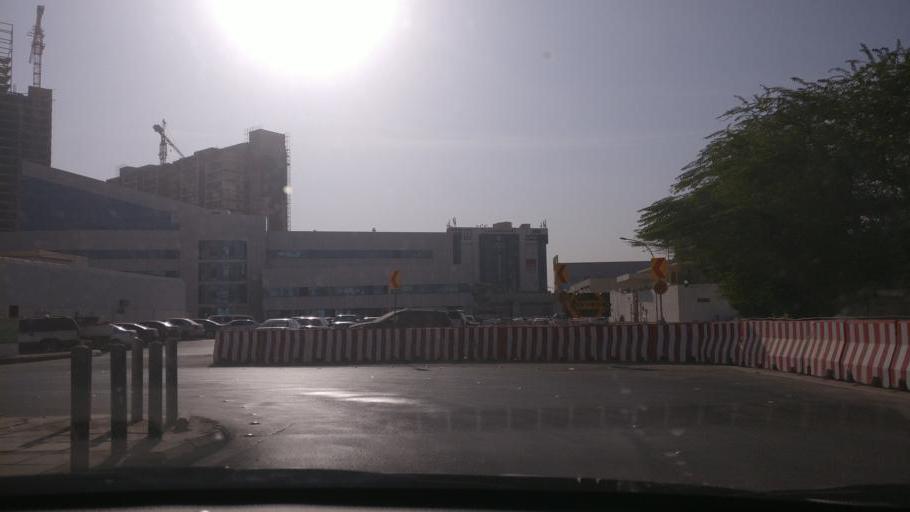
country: SA
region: Ar Riyad
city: Riyadh
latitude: 24.6666
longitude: 46.7009
